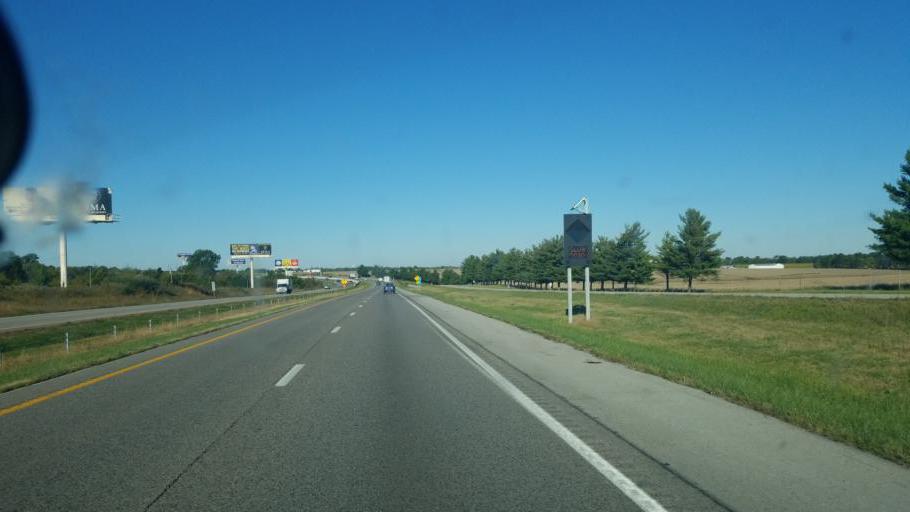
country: US
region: Missouri
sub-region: Gasconade County
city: Hermann
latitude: 38.8674
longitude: -91.3357
